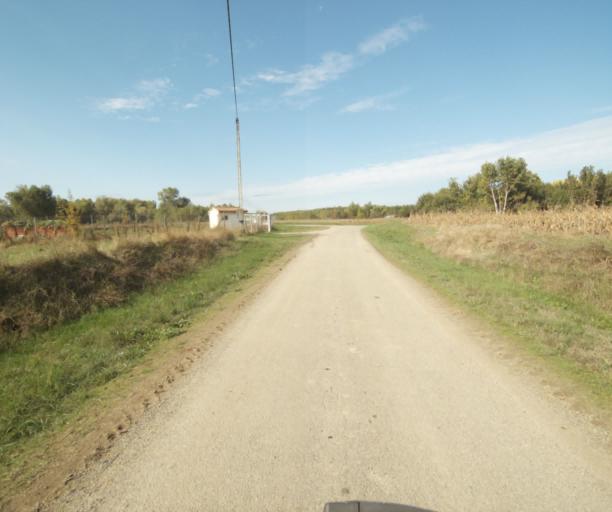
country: FR
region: Midi-Pyrenees
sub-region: Departement du Tarn-et-Garonne
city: Finhan
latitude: 43.9140
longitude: 1.2113
